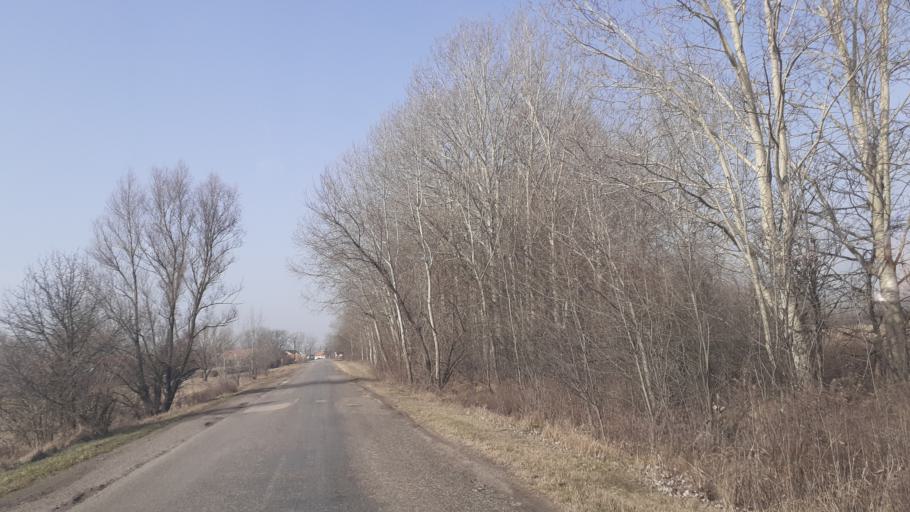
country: HU
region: Pest
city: Dabas
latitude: 47.0625
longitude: 19.2858
